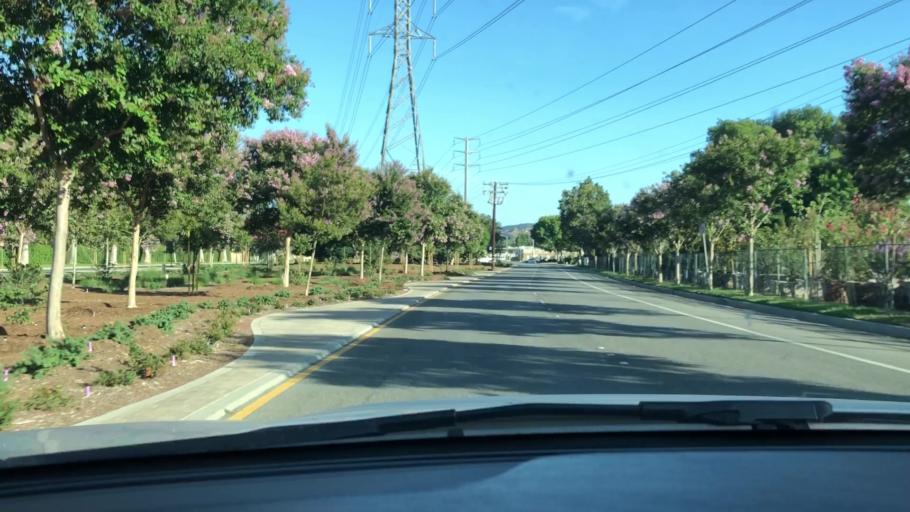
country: US
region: California
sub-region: Los Angeles County
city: Santa Clarita
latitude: 34.3835
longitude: -118.5427
